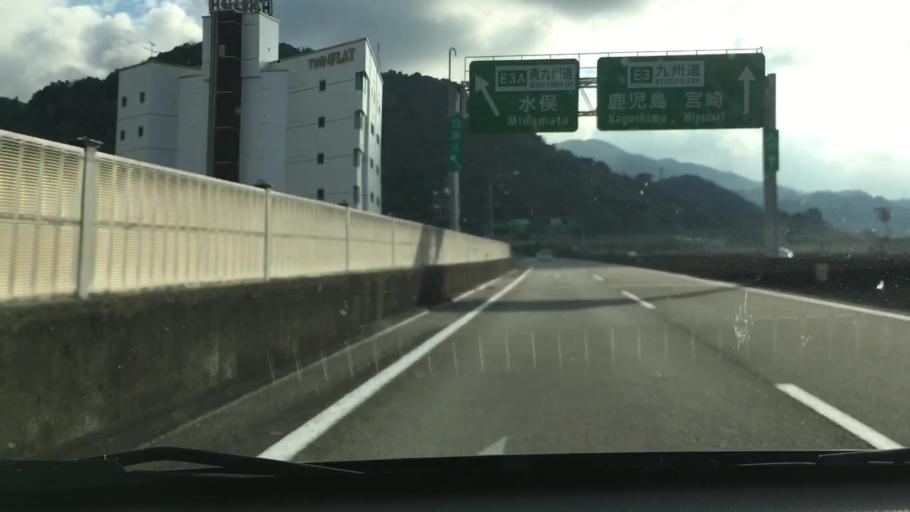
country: JP
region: Kumamoto
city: Yatsushiro
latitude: 32.5070
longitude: 130.6465
